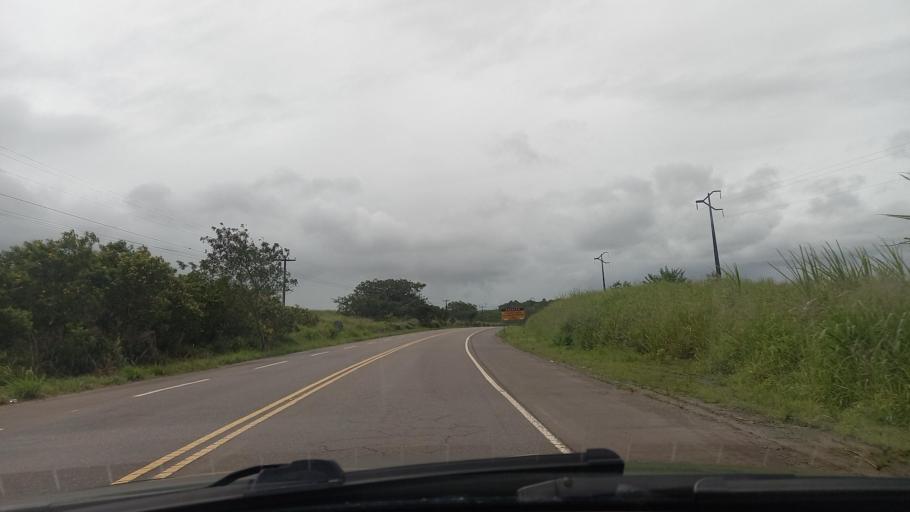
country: BR
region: Alagoas
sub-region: Sao Miguel Dos Campos
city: Sao Miguel dos Campos
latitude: -9.8054
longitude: -36.2072
